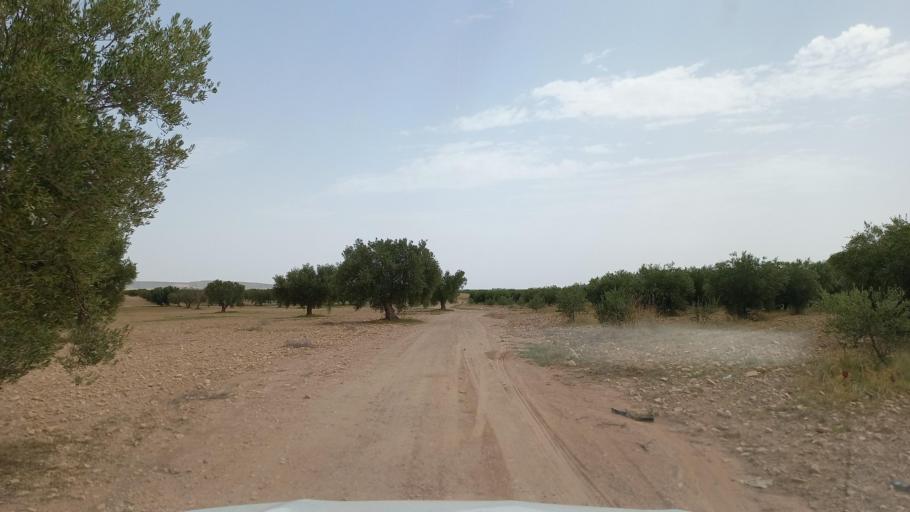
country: TN
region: Al Qasrayn
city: Kasserine
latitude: 35.2893
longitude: 9.0259
